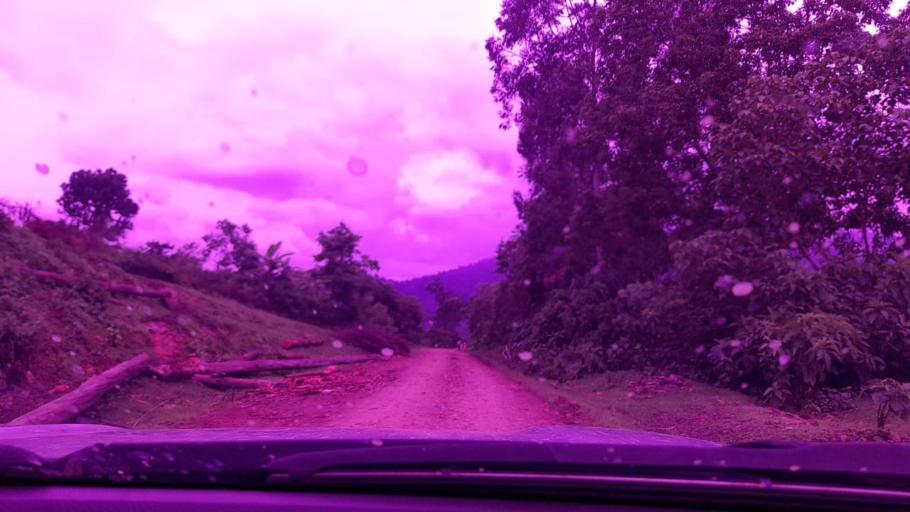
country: ET
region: Southern Nations, Nationalities, and People's Region
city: Bonga
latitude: 7.5478
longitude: 35.8448
